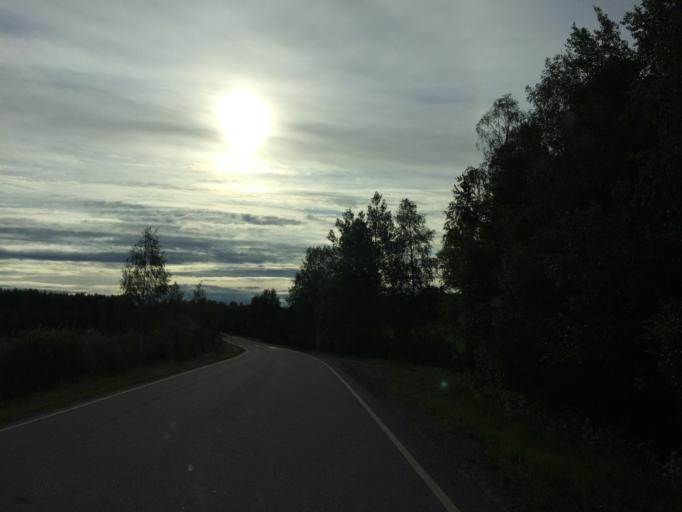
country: FI
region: Haeme
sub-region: Haemeenlinna
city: Janakkala
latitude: 60.8786
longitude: 24.5654
